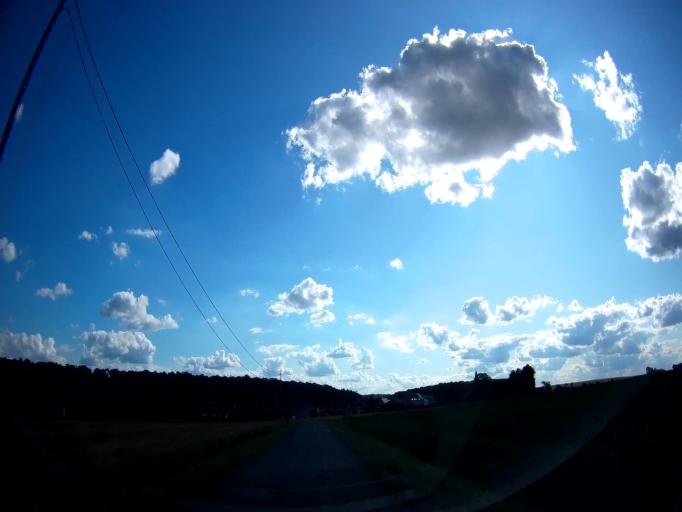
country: BE
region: Wallonia
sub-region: Province de Namur
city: Mettet
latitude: 50.3110
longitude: 4.7107
